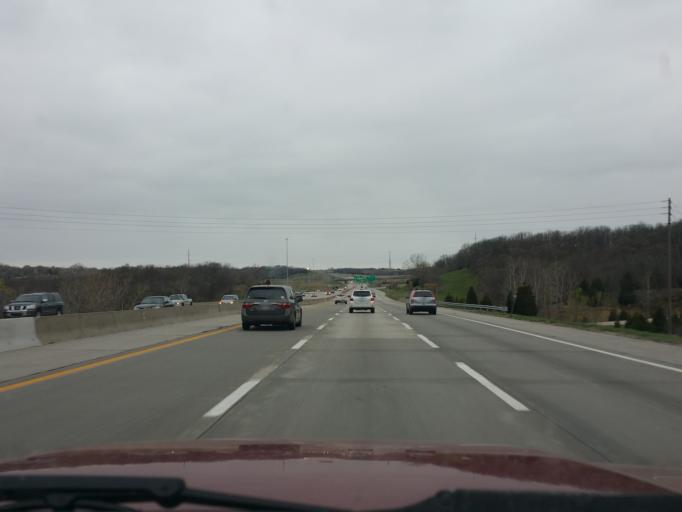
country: US
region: Kansas
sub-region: Wyandotte County
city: Edwardsville
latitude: 39.1056
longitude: -94.7959
